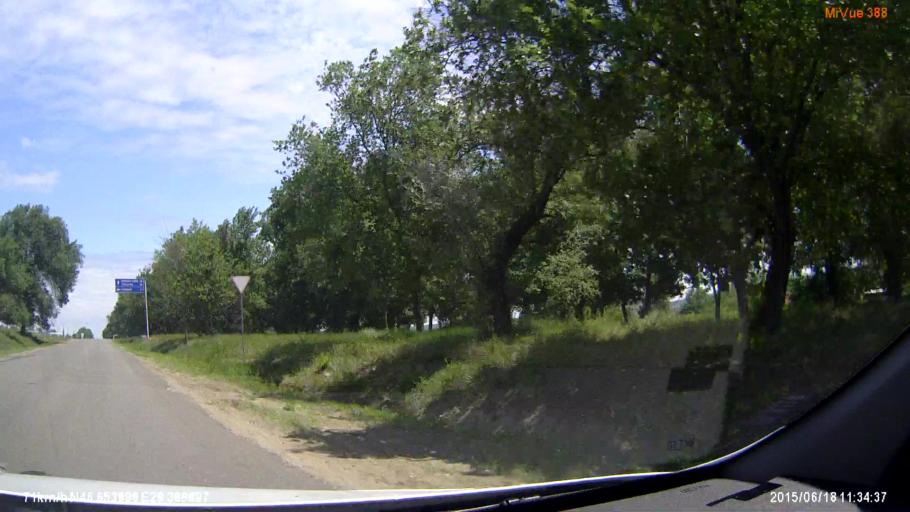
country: MD
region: Causeni
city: Causeni
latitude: 46.6538
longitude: 29.3892
